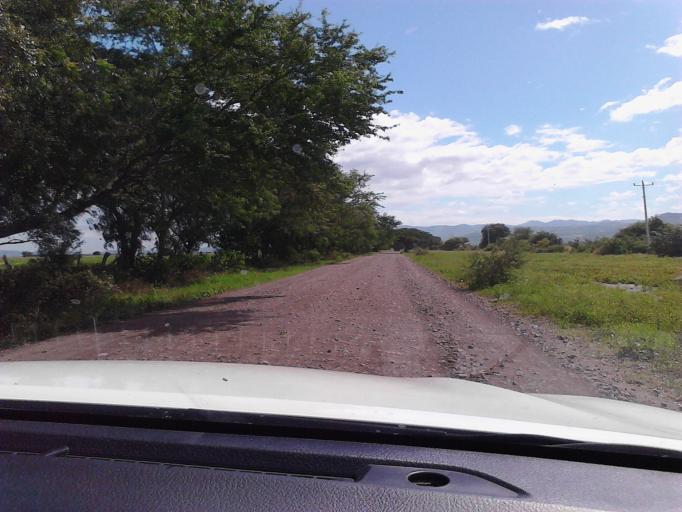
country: NI
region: Matagalpa
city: Ciudad Dario
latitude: 12.8968
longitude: -86.1485
